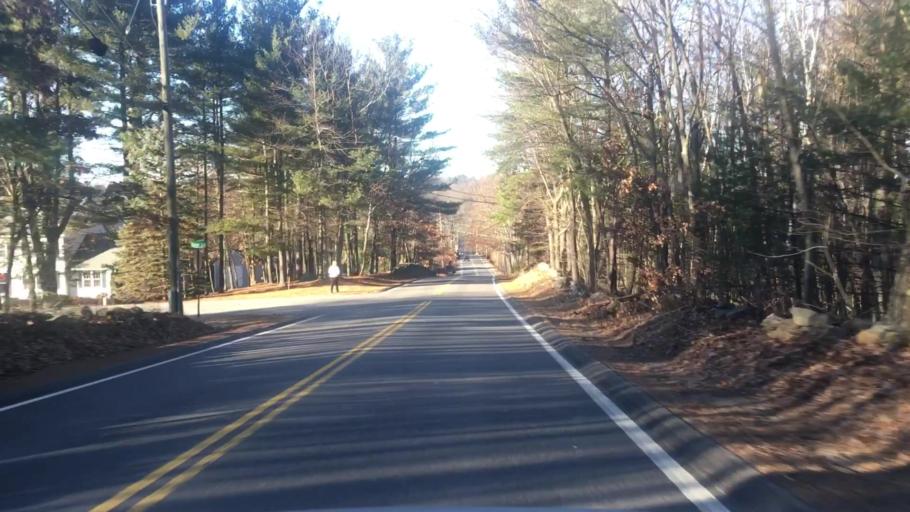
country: US
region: New Hampshire
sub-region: Rockingham County
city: Londonderry
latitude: 42.8934
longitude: -71.3705
